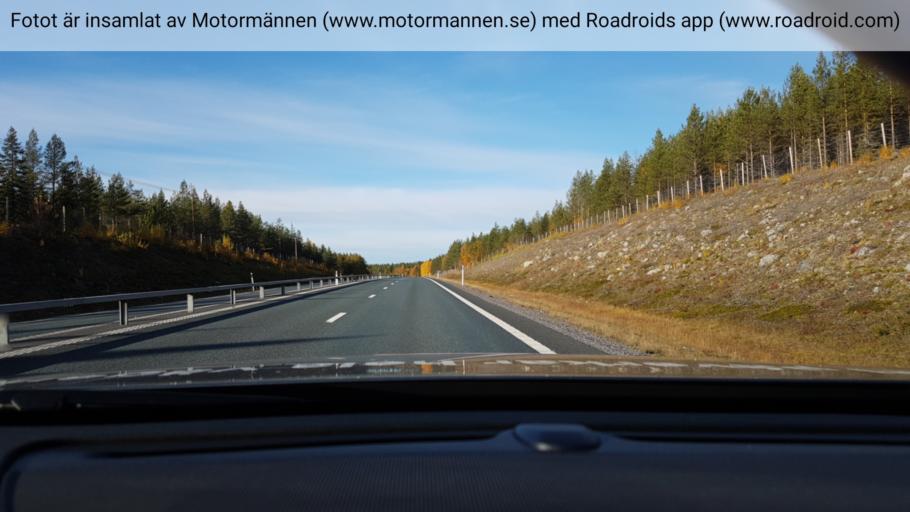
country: SE
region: Norrbotten
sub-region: Kalix Kommun
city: Kalix
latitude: 65.8277
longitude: 23.3466
